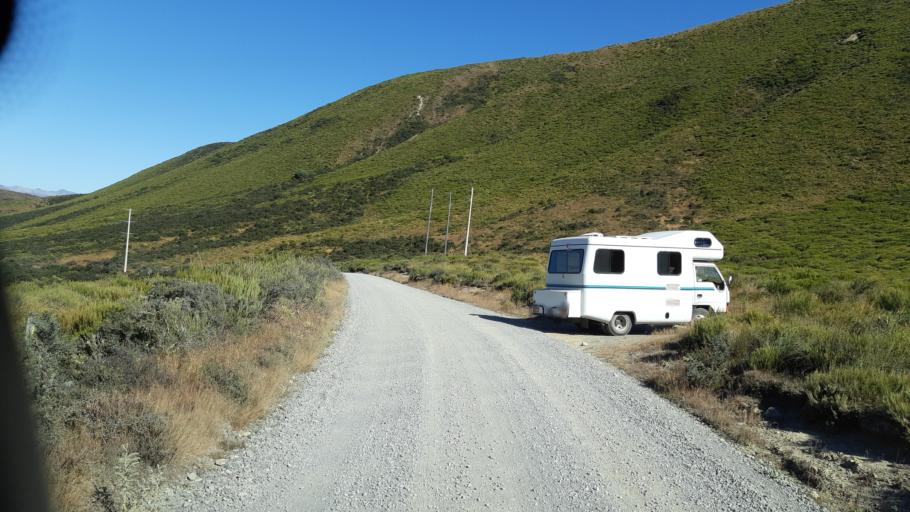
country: NZ
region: Canterbury
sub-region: Ashburton District
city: Methven
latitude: -43.3346
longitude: 171.6583
